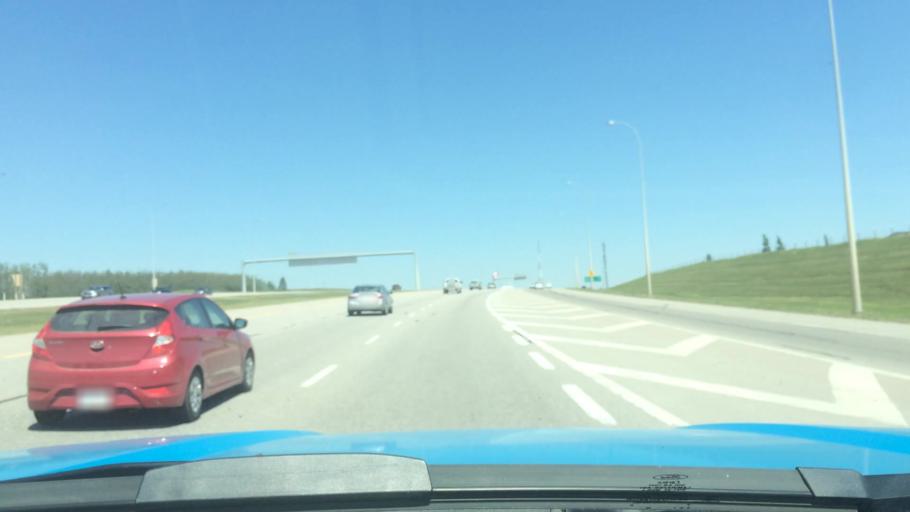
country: CA
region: Alberta
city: Calgary
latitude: 51.1471
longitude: -114.2000
